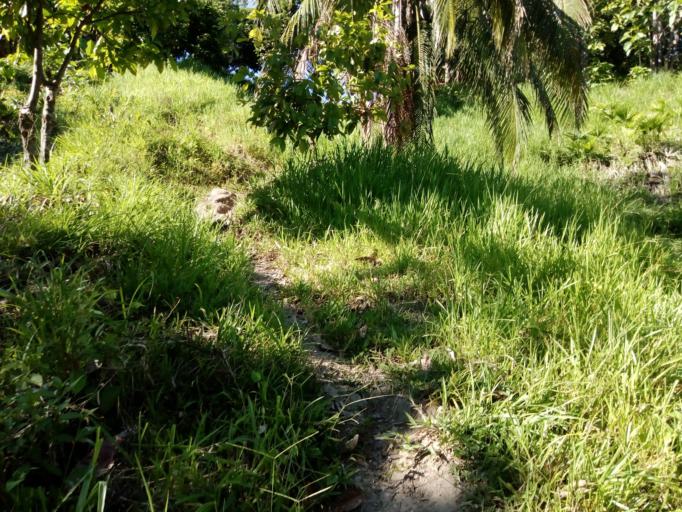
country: CO
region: Boyaca
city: Puerto Boyaca
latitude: 6.0020
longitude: -74.3726
